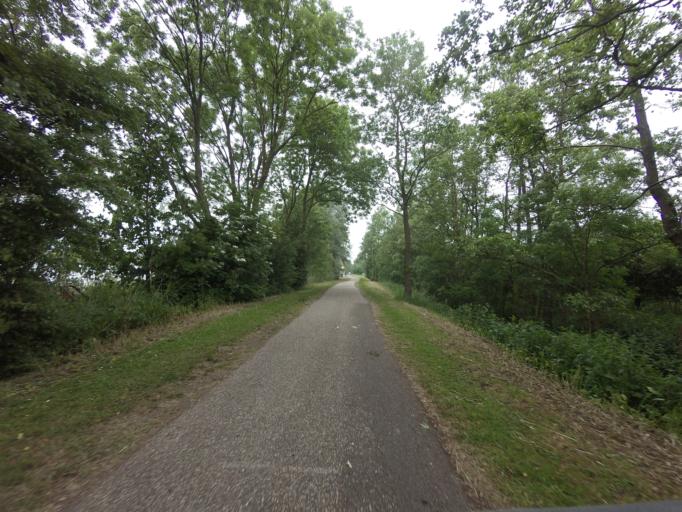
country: NL
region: Utrecht
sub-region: Gemeente Nieuwegein
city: Nieuwegein
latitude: 52.0736
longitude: 5.0593
